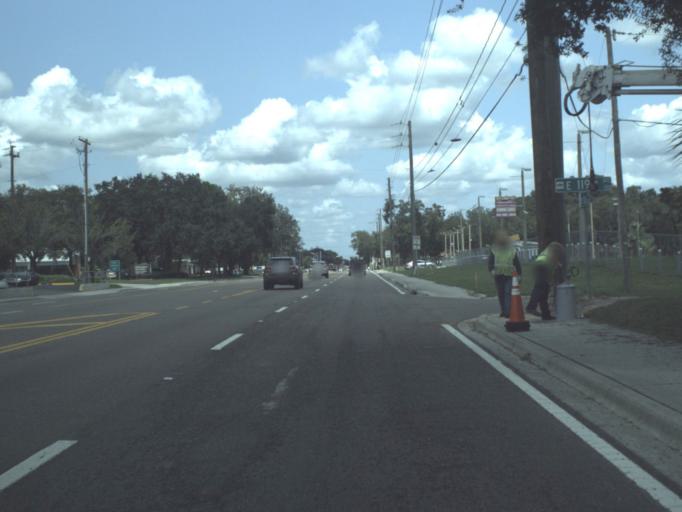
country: US
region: Florida
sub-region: Hillsborough County
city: Lake Magdalene
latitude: 28.0558
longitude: -82.4593
